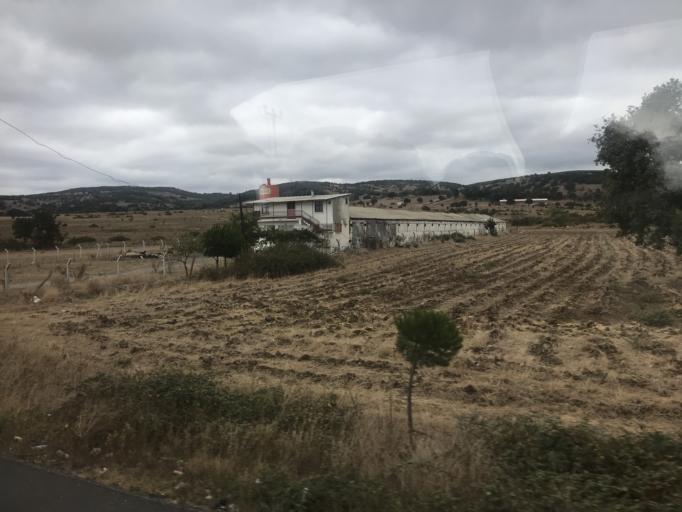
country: TR
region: Balikesir
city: Ergama
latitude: 39.6351
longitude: 27.6596
